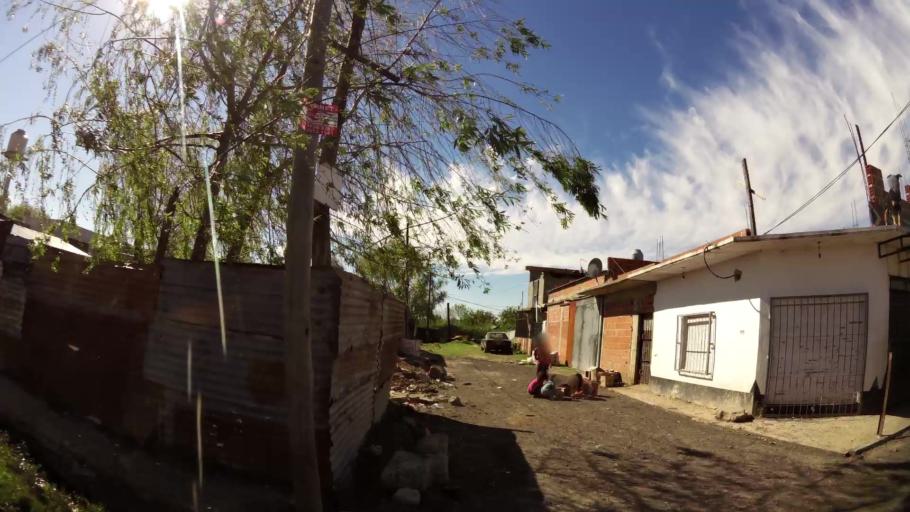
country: AR
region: Buenos Aires
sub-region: Partido de Quilmes
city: Quilmes
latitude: -34.7624
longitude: -58.3104
